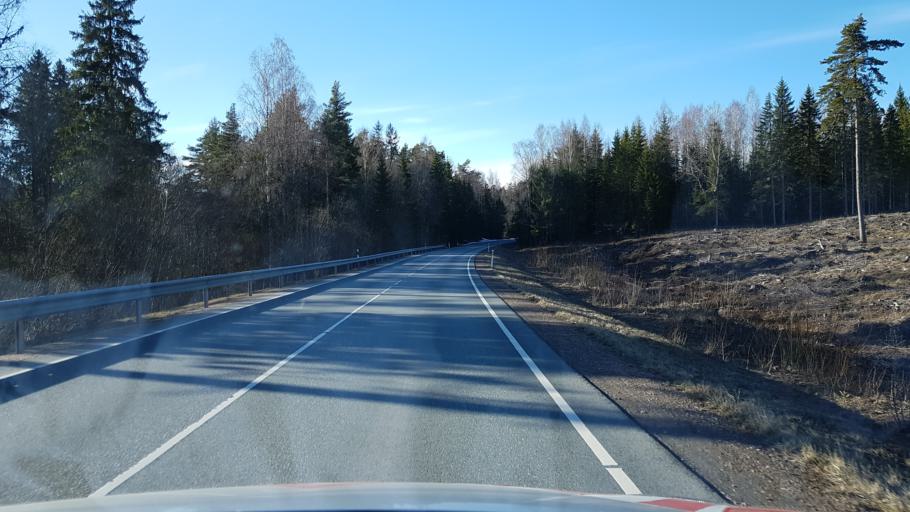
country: EE
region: Laeaene-Virumaa
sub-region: Tapa vald
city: Tapa
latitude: 59.4028
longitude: 26.0077
